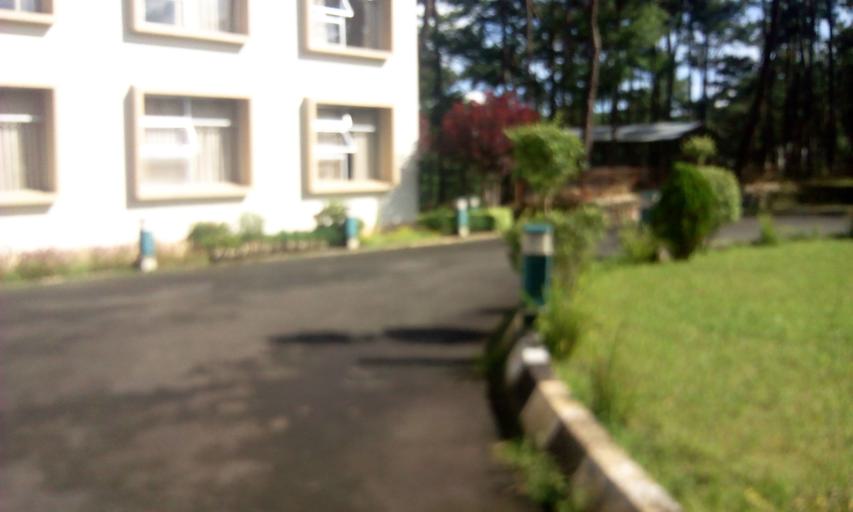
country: IN
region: Meghalaya
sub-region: East Khasi Hills
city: Shillong
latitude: 25.6107
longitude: 91.8937
